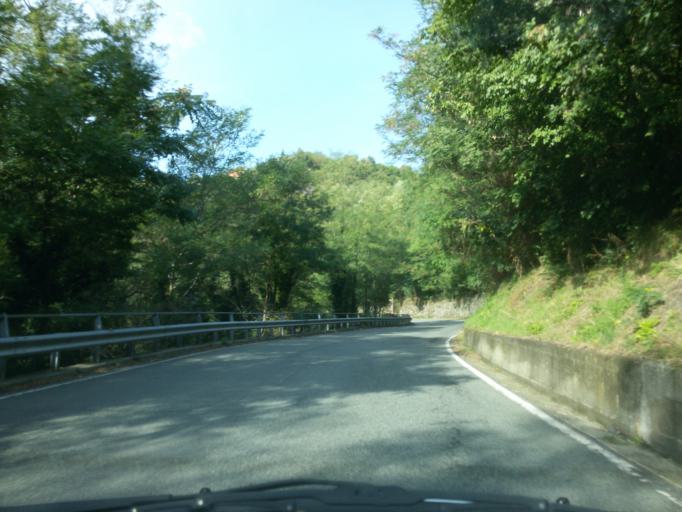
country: IT
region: Liguria
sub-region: Provincia di Genova
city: Piccarello
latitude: 44.4895
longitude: 8.9743
